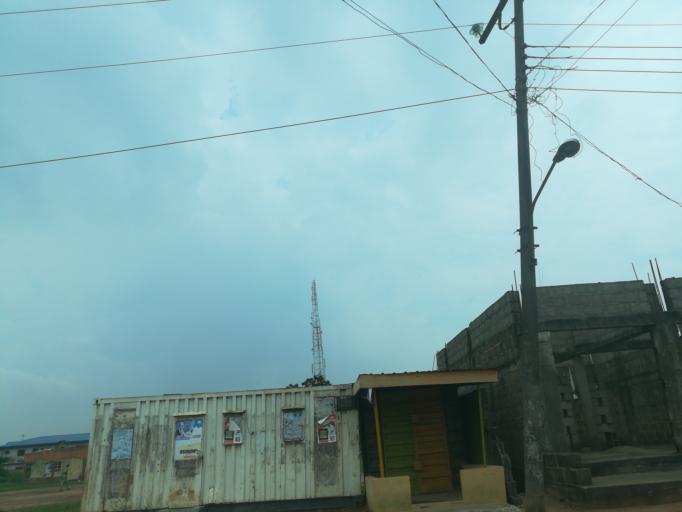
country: NG
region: Lagos
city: Ikorodu
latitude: 6.5674
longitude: 3.5936
